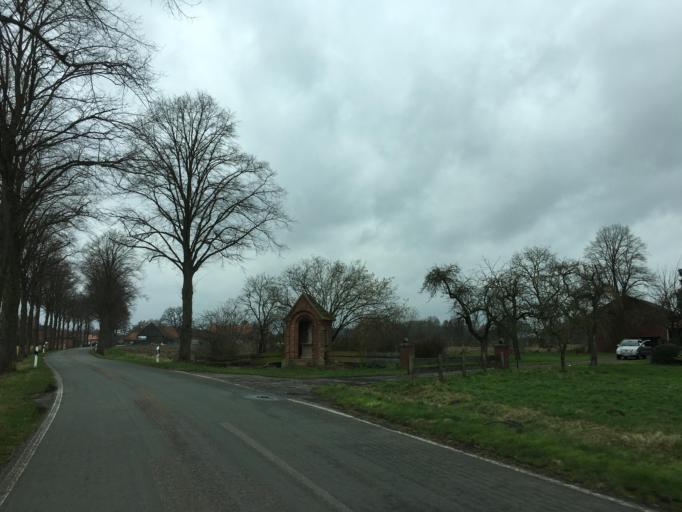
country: DE
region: North Rhine-Westphalia
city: Ludinghausen
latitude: 51.8101
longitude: 7.3979
